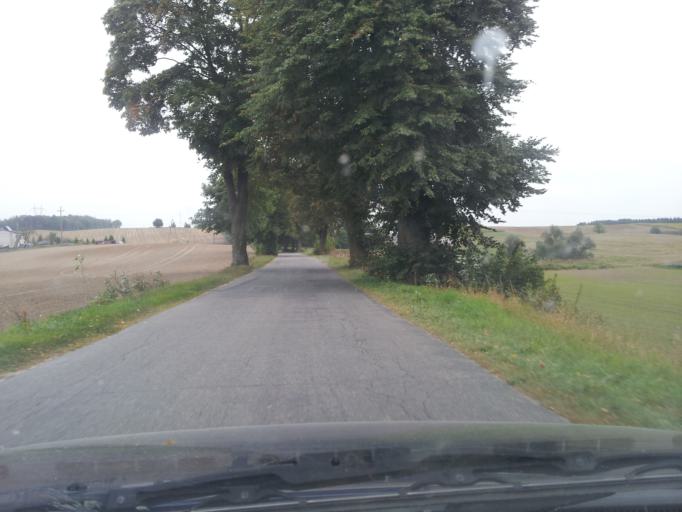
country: PL
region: Kujawsko-Pomorskie
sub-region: Powiat brodnicki
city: Brzozie
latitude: 53.2944
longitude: 19.6711
